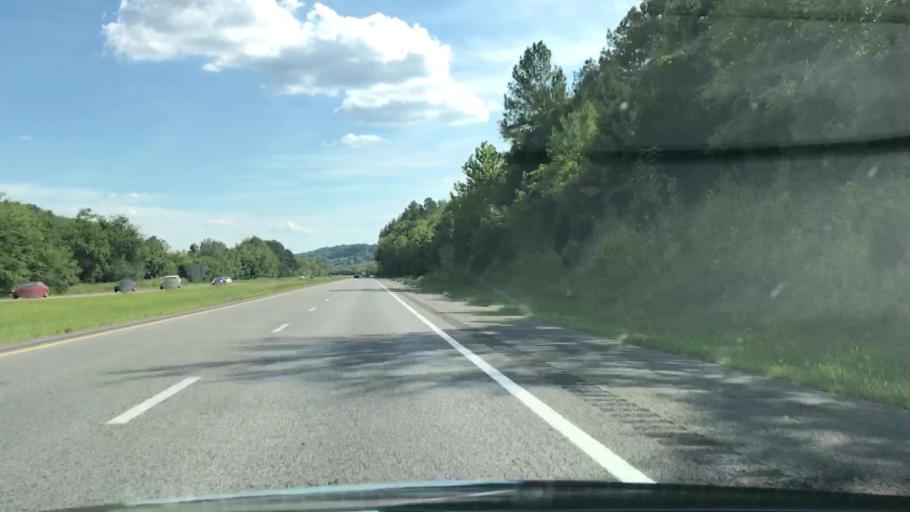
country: US
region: Tennessee
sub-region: Giles County
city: Pulaski
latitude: 35.1708
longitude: -86.8786
